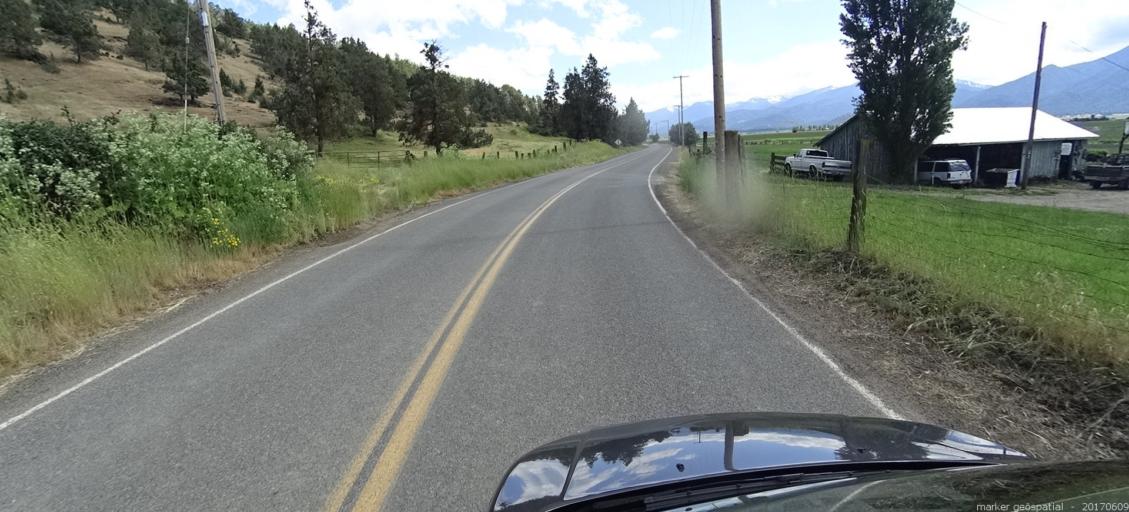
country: US
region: California
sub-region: Siskiyou County
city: Yreka
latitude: 41.5158
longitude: -122.8394
